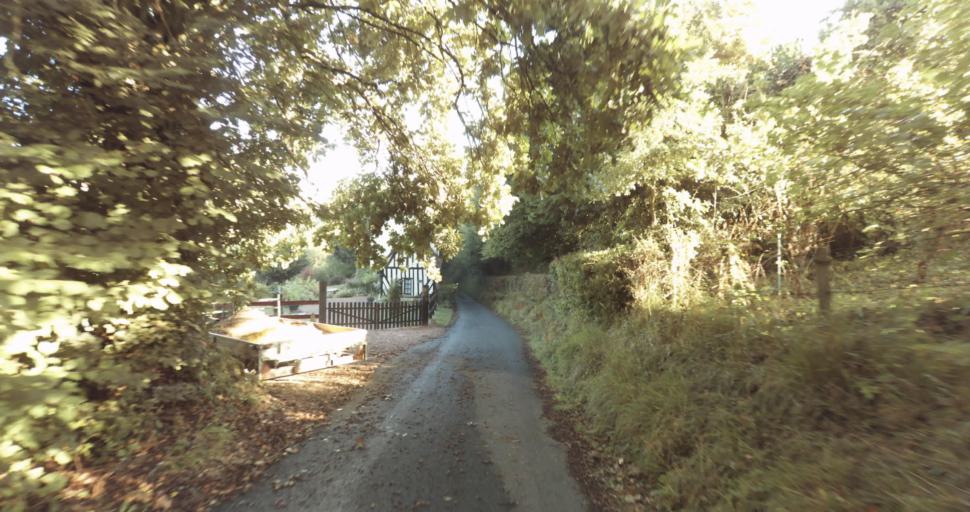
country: FR
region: Lower Normandy
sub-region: Departement de l'Orne
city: Vimoutiers
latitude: 48.9202
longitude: 0.1739
